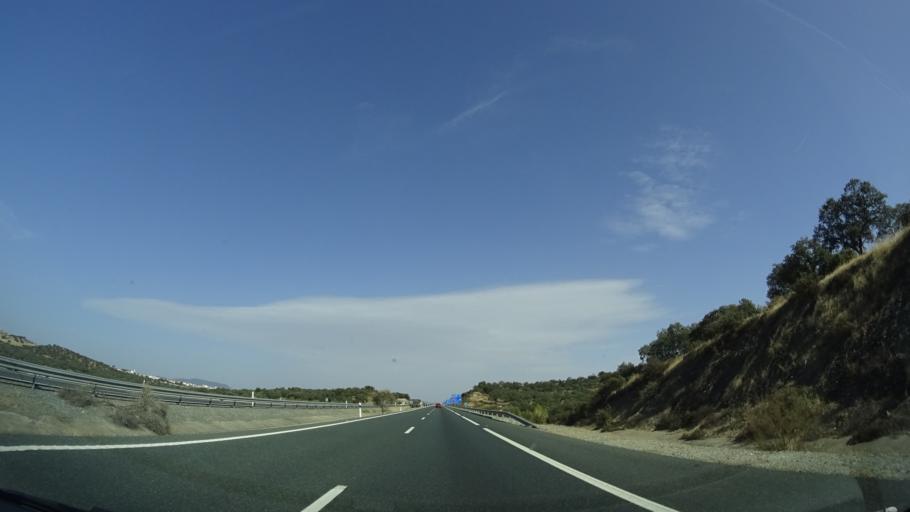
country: ES
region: Andalusia
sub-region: Provincia de Huelva
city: Santa Olalla del Cala
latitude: 37.8899
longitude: -6.2171
